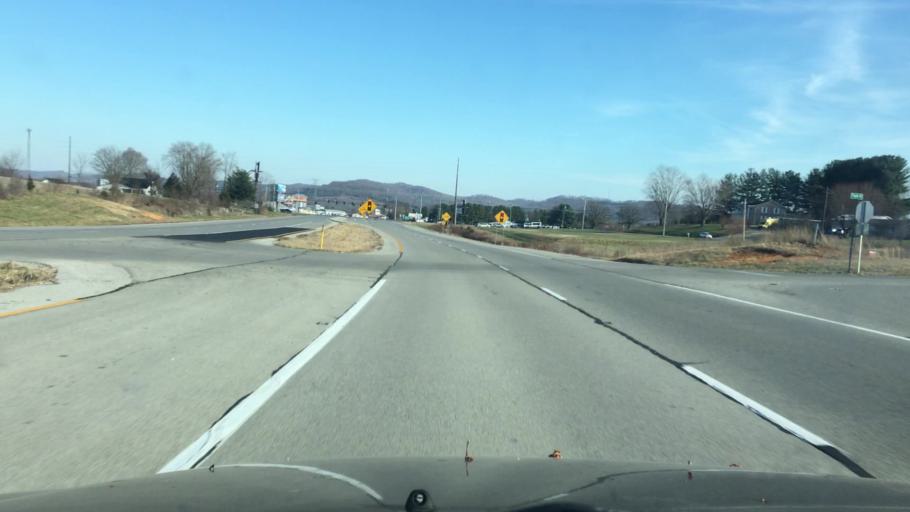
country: US
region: Kentucky
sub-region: Pulaski County
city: Somerset
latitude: 37.0288
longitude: -84.6317
